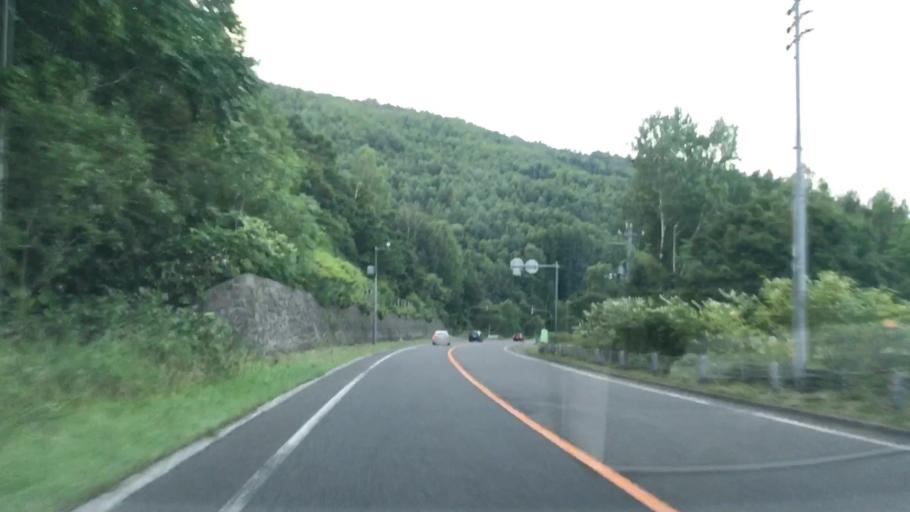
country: JP
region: Hokkaido
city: Sapporo
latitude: 42.9089
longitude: 141.1204
